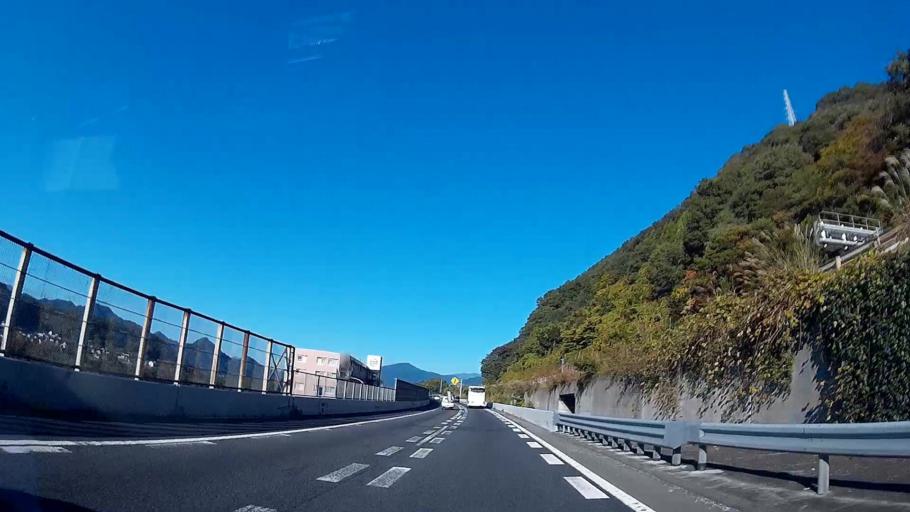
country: JP
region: Yamanashi
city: Uenohara
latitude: 35.6169
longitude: 139.1472
